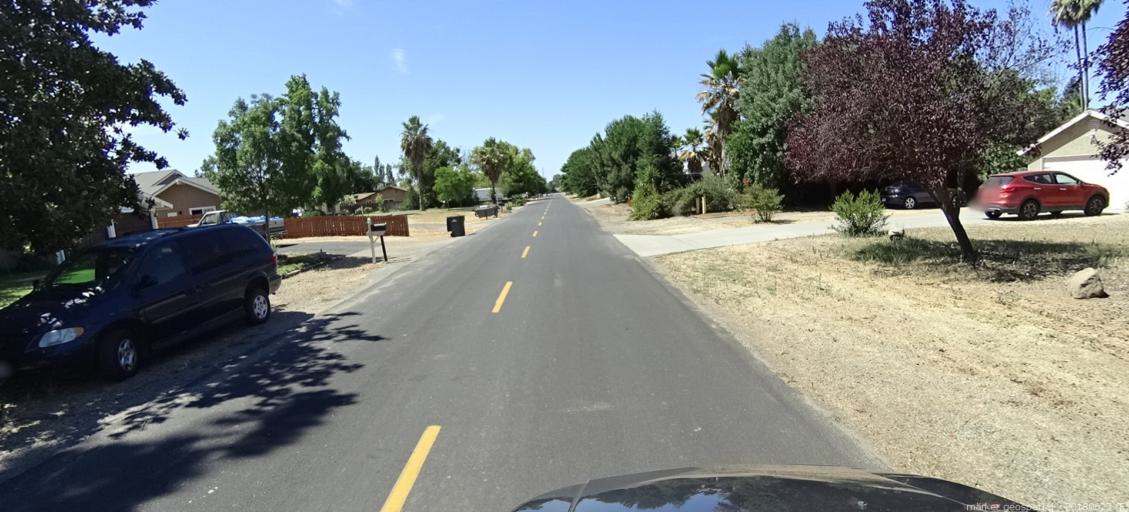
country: US
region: California
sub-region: Madera County
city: Bonadelle Ranchos-Madera Ranchos
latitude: 36.9269
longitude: -119.8780
